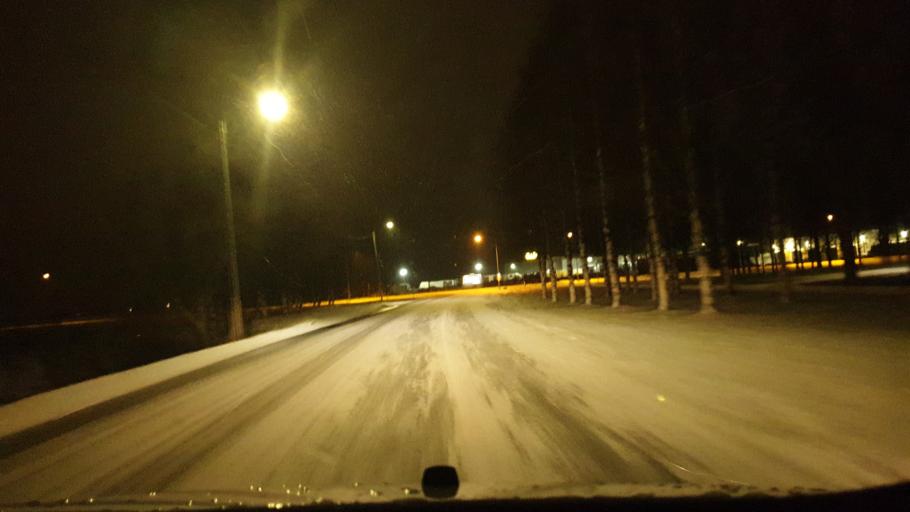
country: FI
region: Northern Ostrobothnia
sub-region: Oulu
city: Oulu
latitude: 64.9903
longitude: 25.4366
